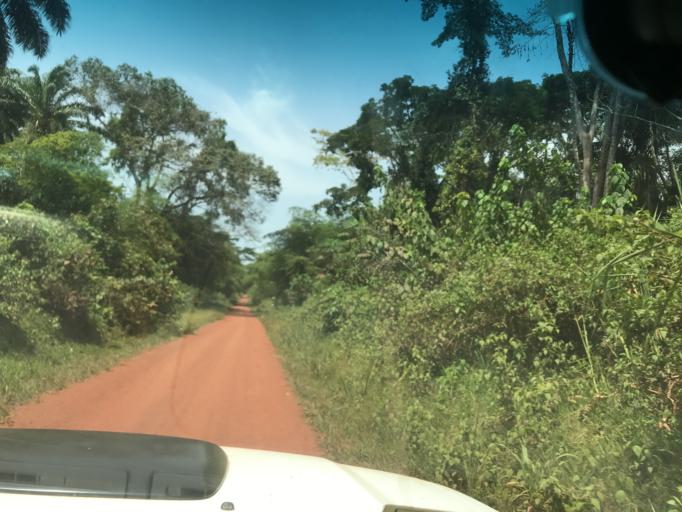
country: CD
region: Eastern Province
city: Aketi
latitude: 2.8736
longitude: 23.9526
